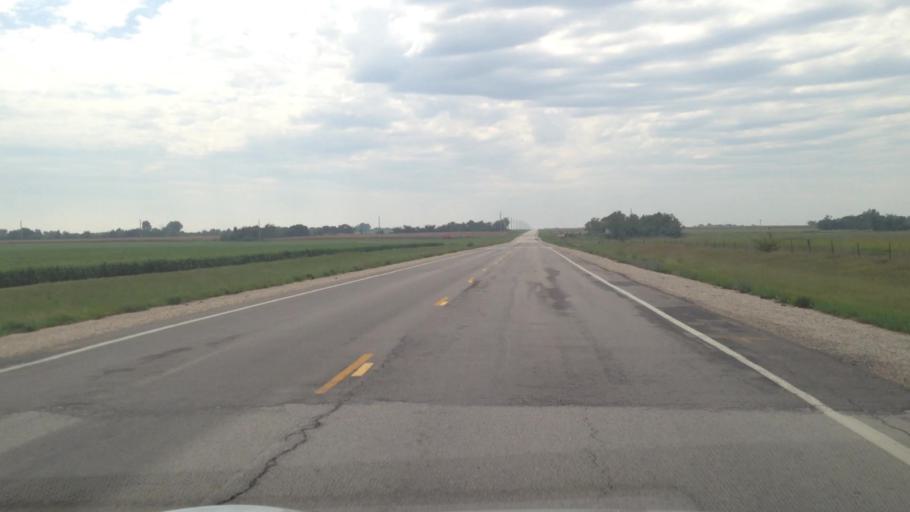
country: US
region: Kansas
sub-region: Anderson County
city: Garnett
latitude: 38.0727
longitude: -95.1694
